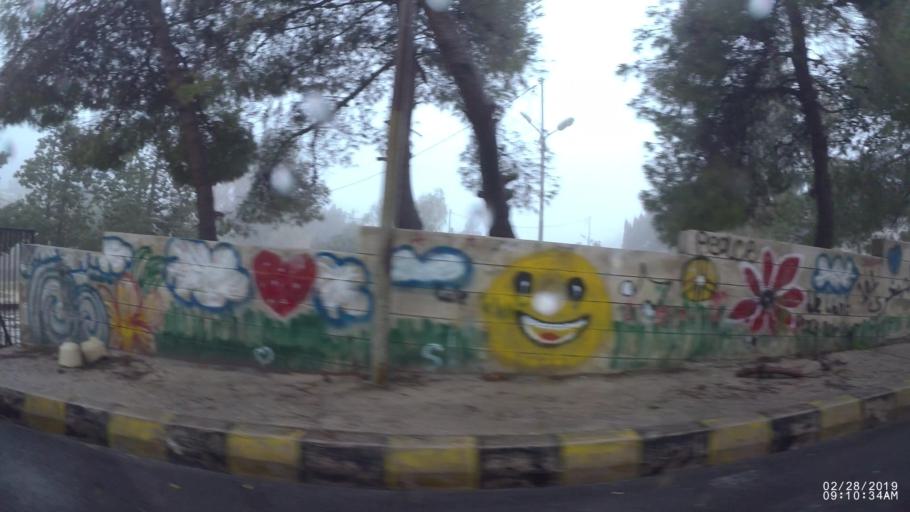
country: JO
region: Amman
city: Al Jubayhah
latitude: 32.0131
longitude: 35.8786
